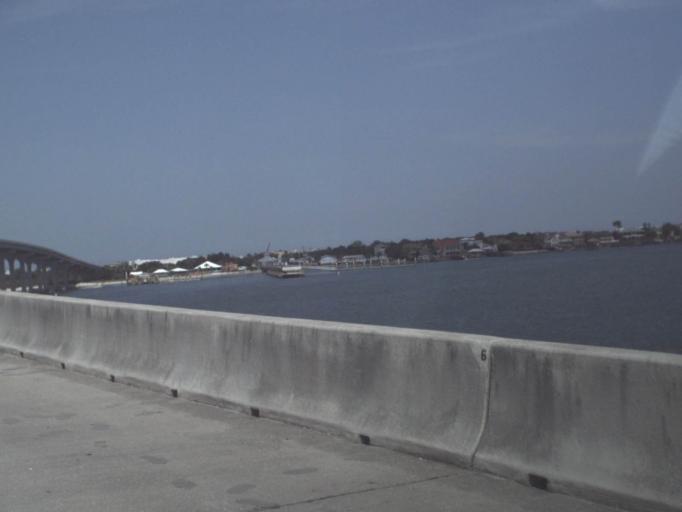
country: US
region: Florida
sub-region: Saint Johns County
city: Villano Beach
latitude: 29.9169
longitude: -81.3047
